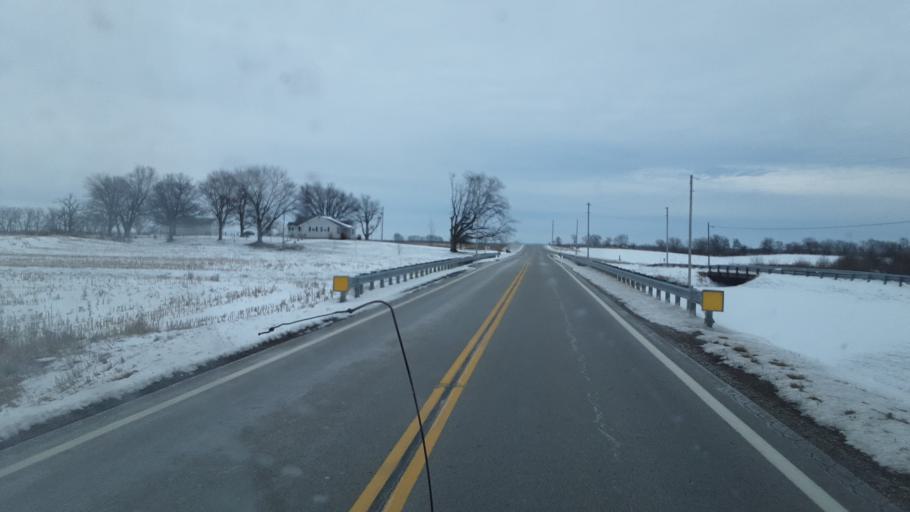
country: US
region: Ohio
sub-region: Pickaway County
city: Williamsport
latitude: 39.6248
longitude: -83.0520
